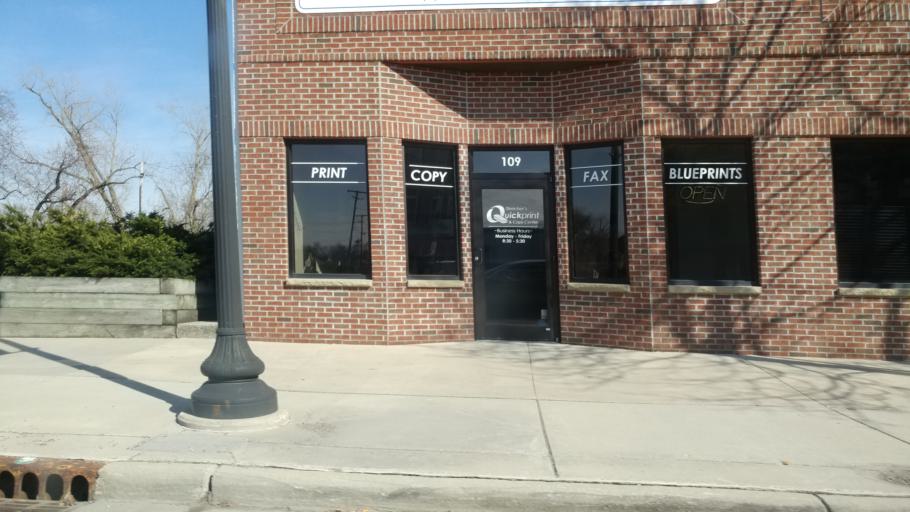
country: US
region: Ohio
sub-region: Hancock County
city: Findlay
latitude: 41.0408
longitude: -83.6500
